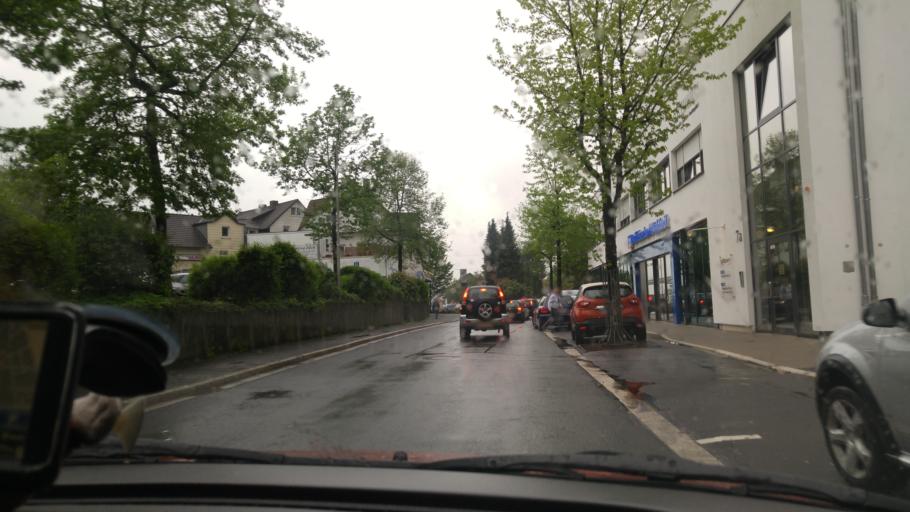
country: DE
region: North Rhine-Westphalia
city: Waldbrol
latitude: 50.8740
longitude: 7.6149
